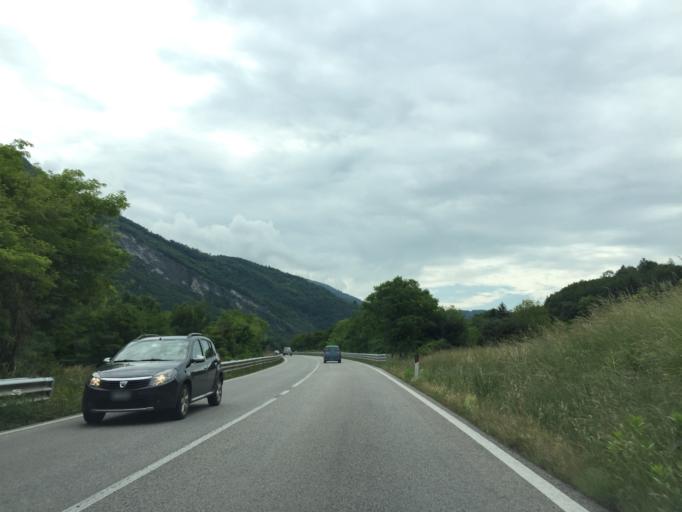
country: IT
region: Veneto
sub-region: Provincia di Belluno
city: Vas
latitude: 45.9327
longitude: 11.9278
